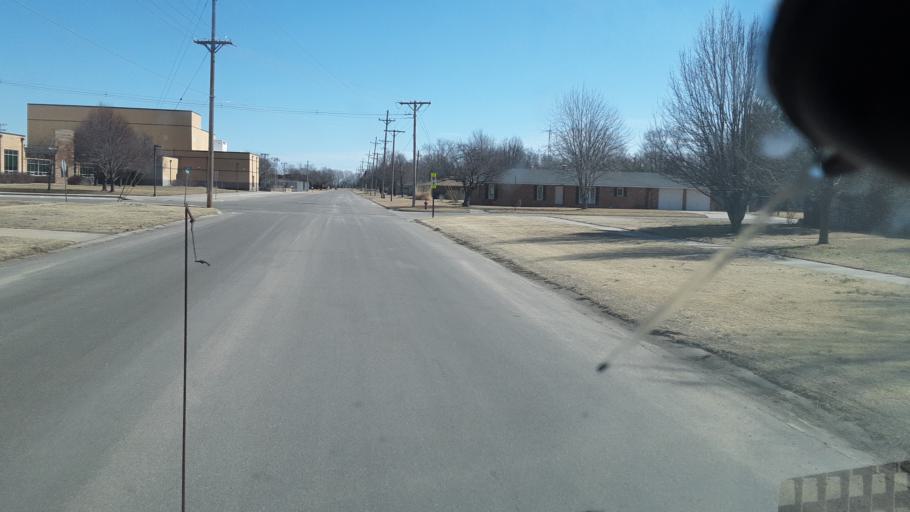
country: US
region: Kansas
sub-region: Rice County
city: Sterling
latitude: 38.2147
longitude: -98.2046
